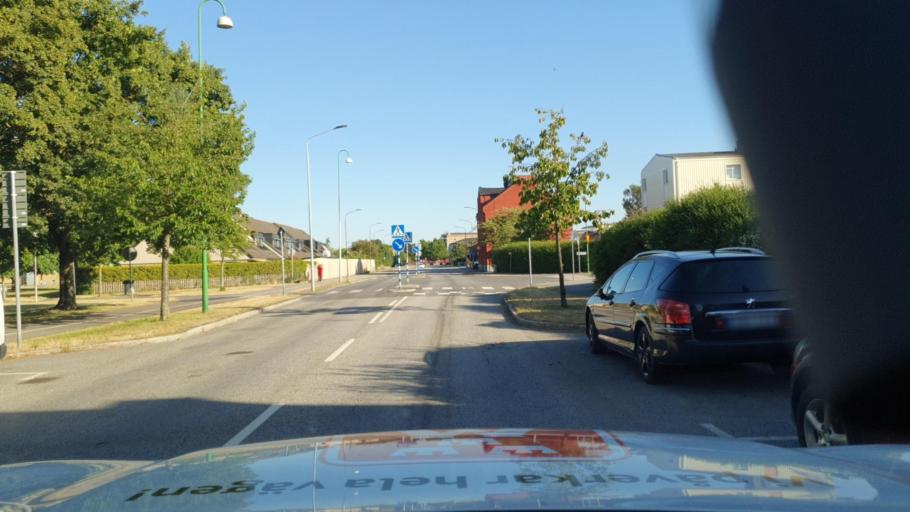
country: SE
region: Skane
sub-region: Burlovs Kommun
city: Arloev
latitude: 55.6375
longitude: 13.0650
